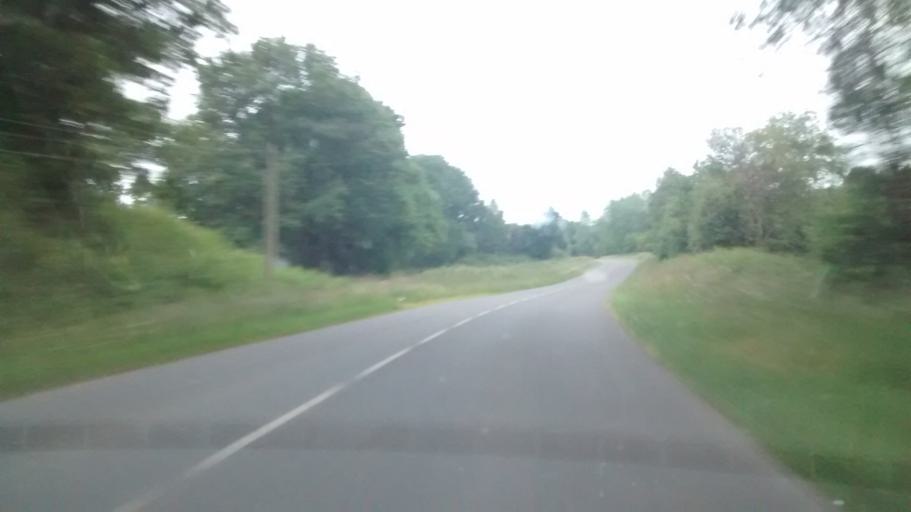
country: FR
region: Brittany
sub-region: Departement du Morbihan
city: Saint-Martin-sur-Oust
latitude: 47.7364
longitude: -2.2763
